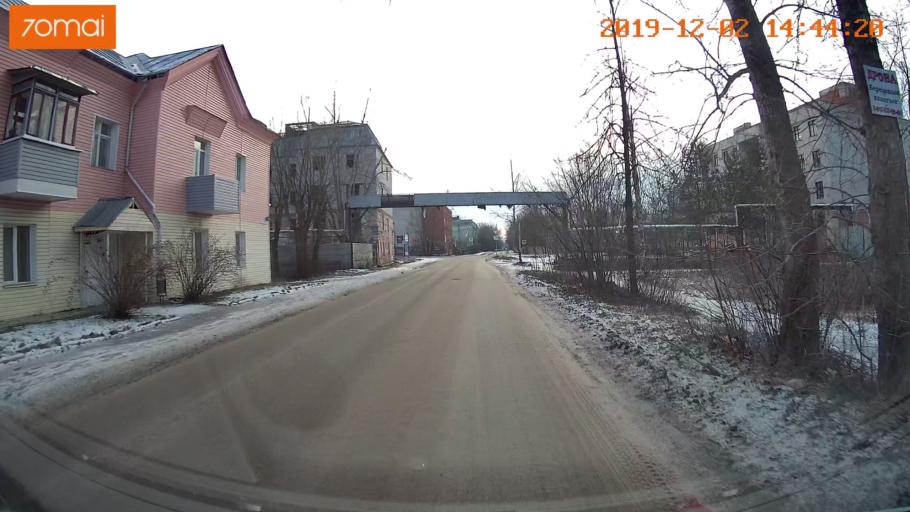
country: RU
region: Ivanovo
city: Bogorodskoye
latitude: 56.9901
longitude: 41.0380
